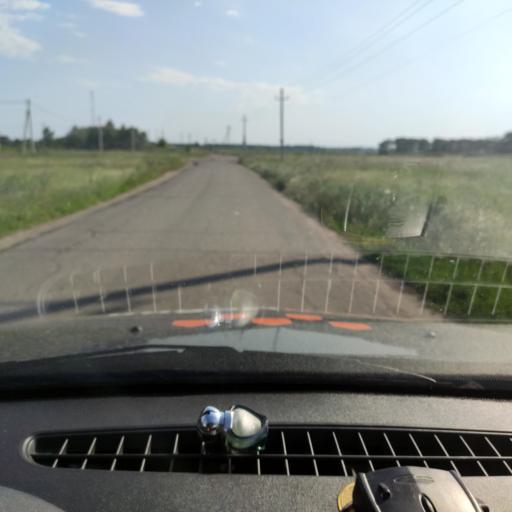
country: RU
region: Voronezj
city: Podkletnoye
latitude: 51.6160
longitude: 39.4390
